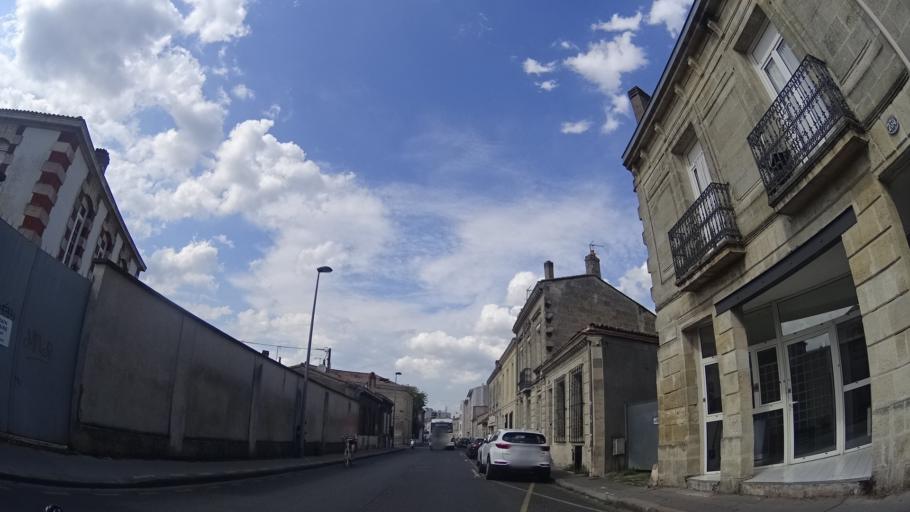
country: FR
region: Aquitaine
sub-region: Departement de la Gironde
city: Begles
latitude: 44.8195
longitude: -0.5661
